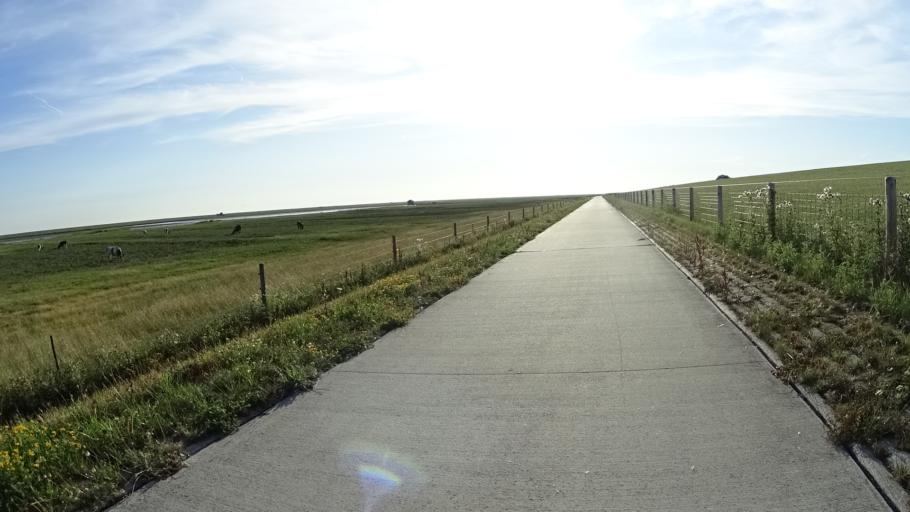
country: DE
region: Lower Saxony
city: Butjadingen
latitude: 53.6094
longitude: 8.3065
